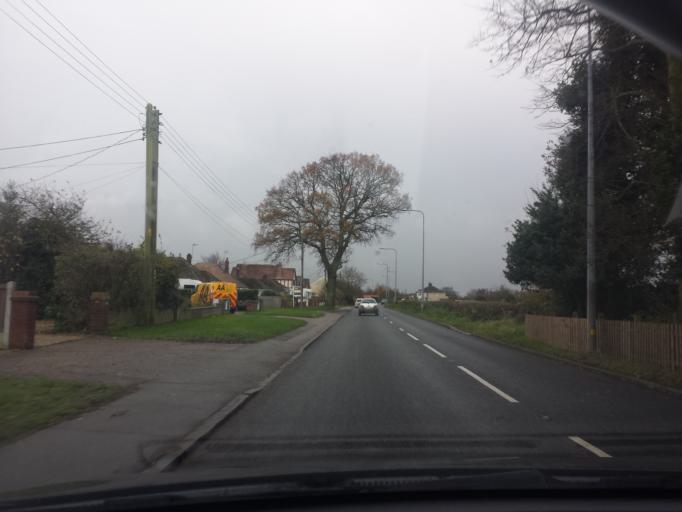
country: GB
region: England
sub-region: Essex
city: Little Clacton
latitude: 51.8337
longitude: 1.1393
